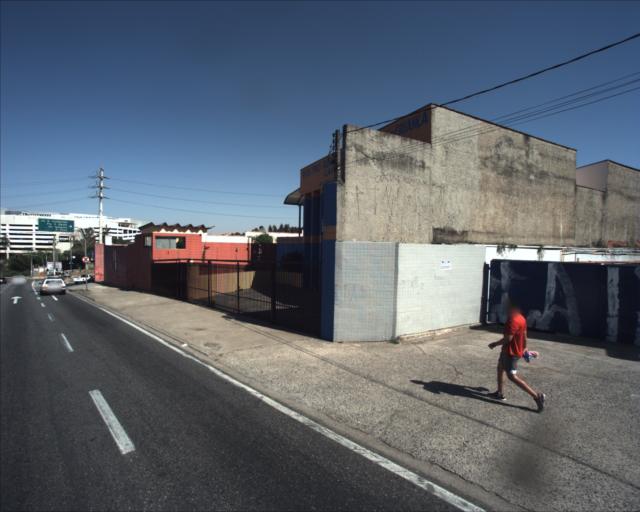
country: BR
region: Sao Paulo
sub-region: Sorocaba
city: Sorocaba
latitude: -23.4535
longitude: -47.4828
